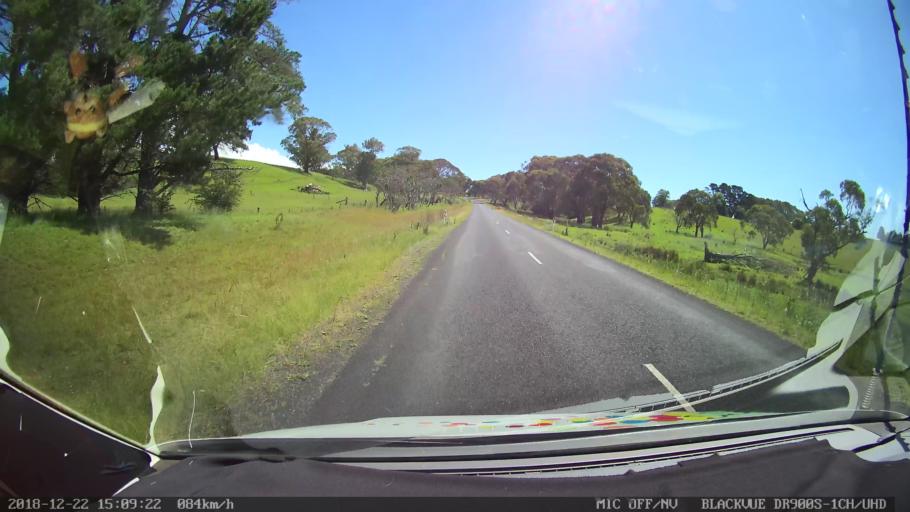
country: AU
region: New South Wales
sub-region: Bellingen
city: Dorrigo
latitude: -30.3234
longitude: 152.4096
